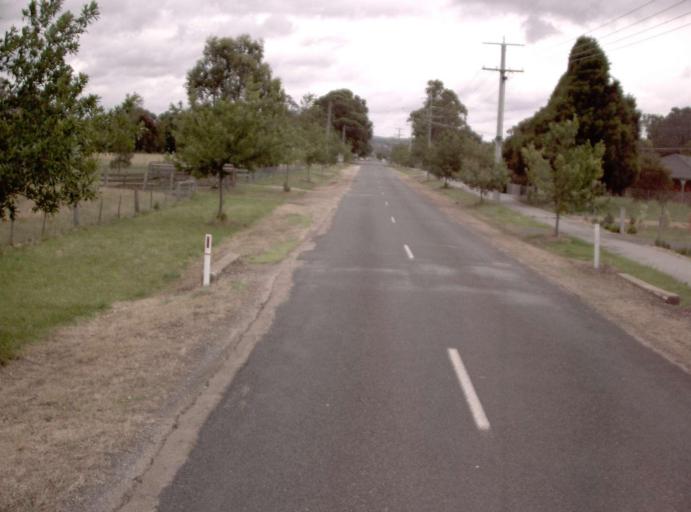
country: AU
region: Victoria
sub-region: Wellington
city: Sale
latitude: -37.8472
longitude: 147.0719
